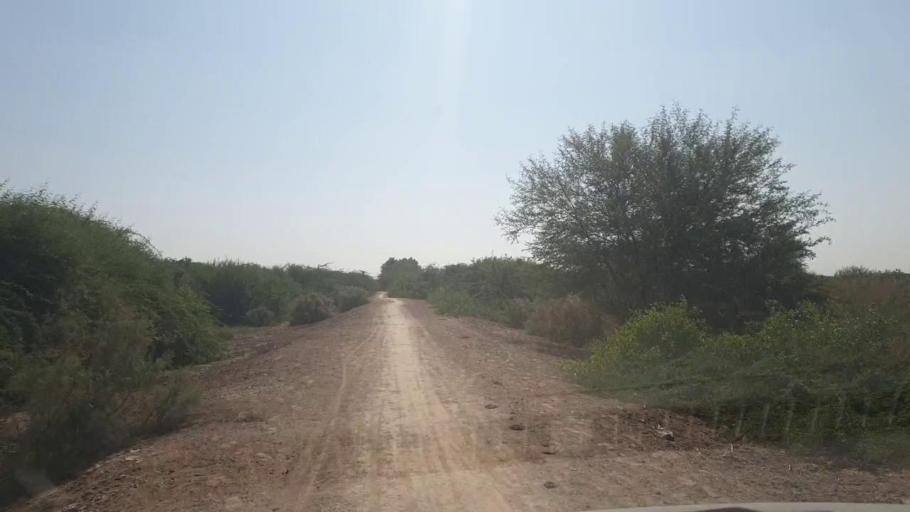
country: PK
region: Sindh
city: Tando Bago
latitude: 24.9010
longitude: 69.1645
